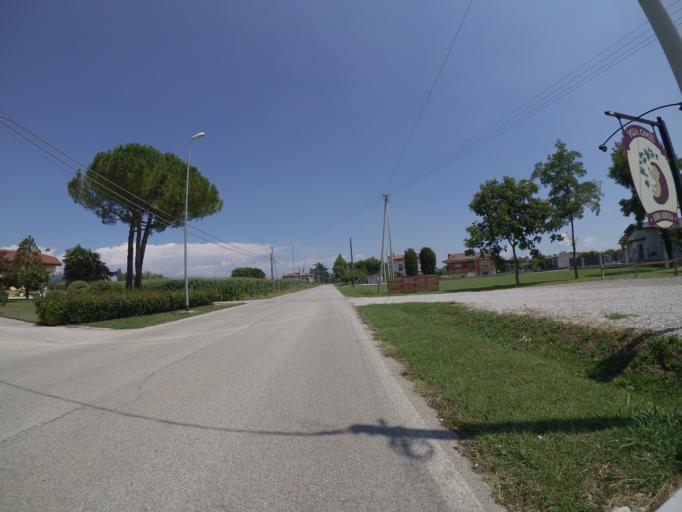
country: IT
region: Friuli Venezia Giulia
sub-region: Provincia di Udine
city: Bertiolo
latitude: 45.9747
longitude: 13.0754
